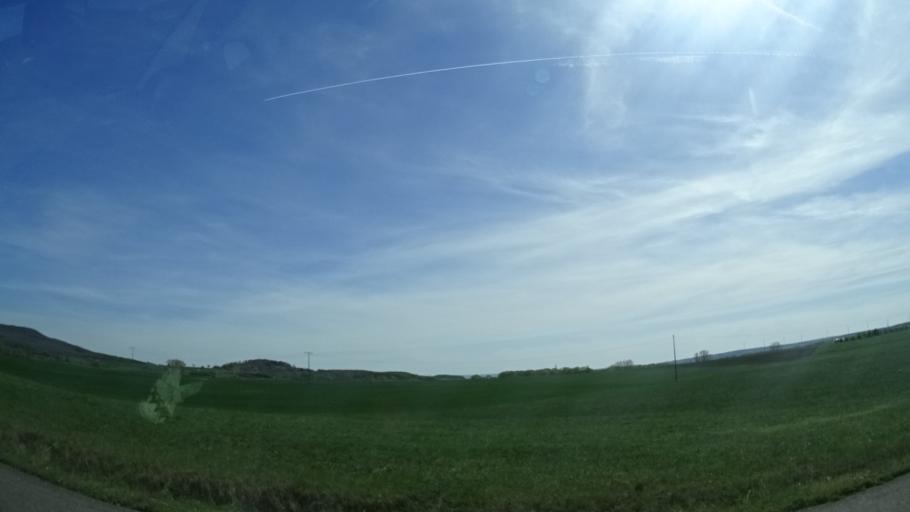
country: DE
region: Bavaria
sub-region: Regierungsbezirk Unterfranken
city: Hofheim in Unterfranken
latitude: 50.1386
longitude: 10.5425
